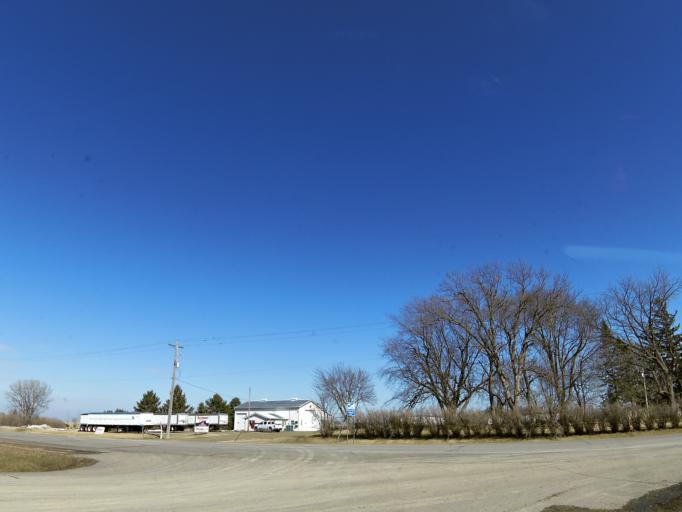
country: US
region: Minnesota
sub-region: Waseca County
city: New Richland
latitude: 43.8924
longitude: -93.4868
